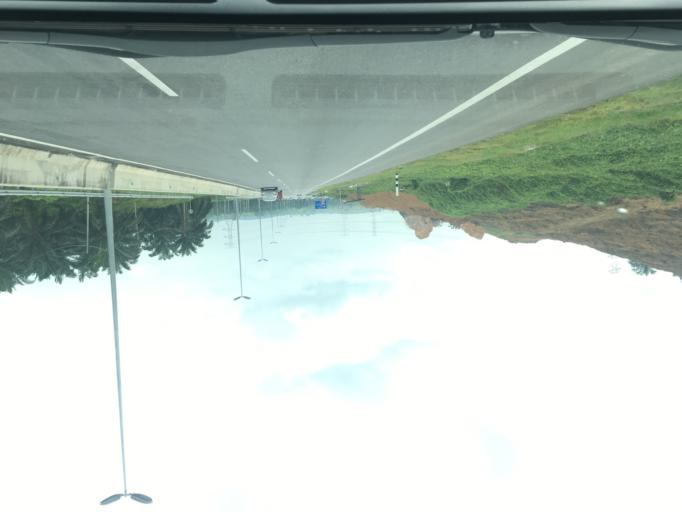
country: MY
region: Selangor
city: Batu Arang
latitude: 3.2911
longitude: 101.4412
